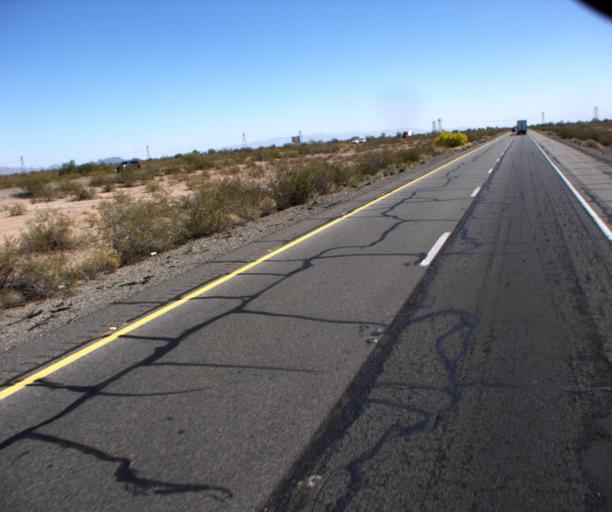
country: US
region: Arizona
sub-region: Maricopa County
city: Buckeye
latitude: 33.5169
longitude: -113.0499
